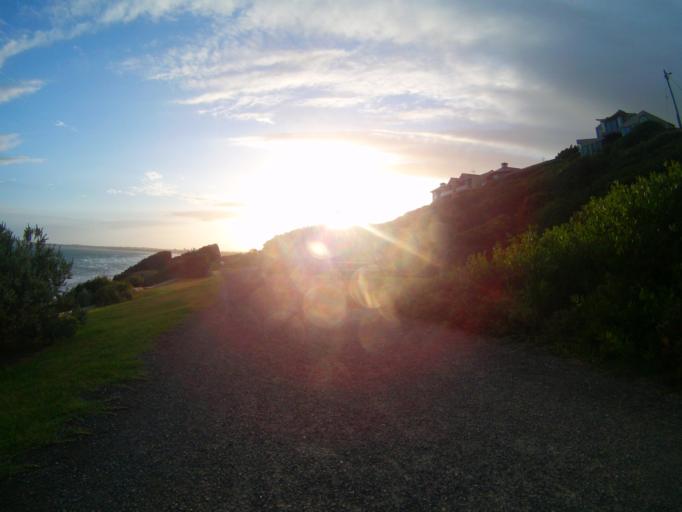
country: AU
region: Victoria
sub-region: Greater Geelong
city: Leopold
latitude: -38.2714
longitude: 144.5225
